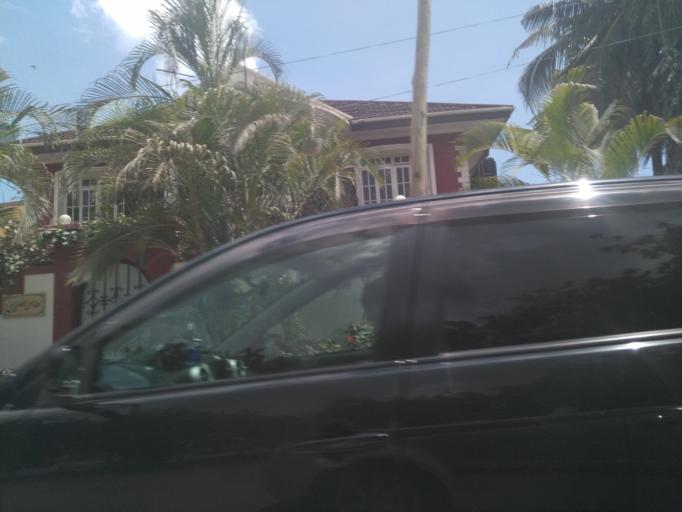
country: TZ
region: Dar es Salaam
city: Dar es Salaam
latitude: -6.8494
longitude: 39.2689
